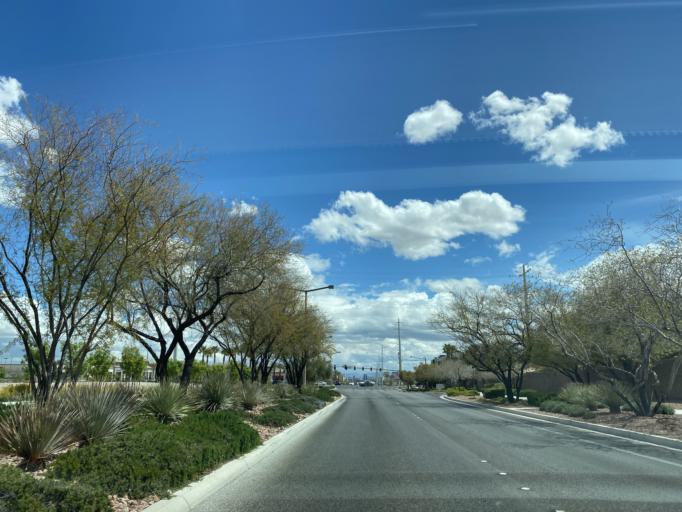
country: US
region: Nevada
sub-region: Clark County
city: Summerlin South
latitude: 36.1152
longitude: -115.3172
